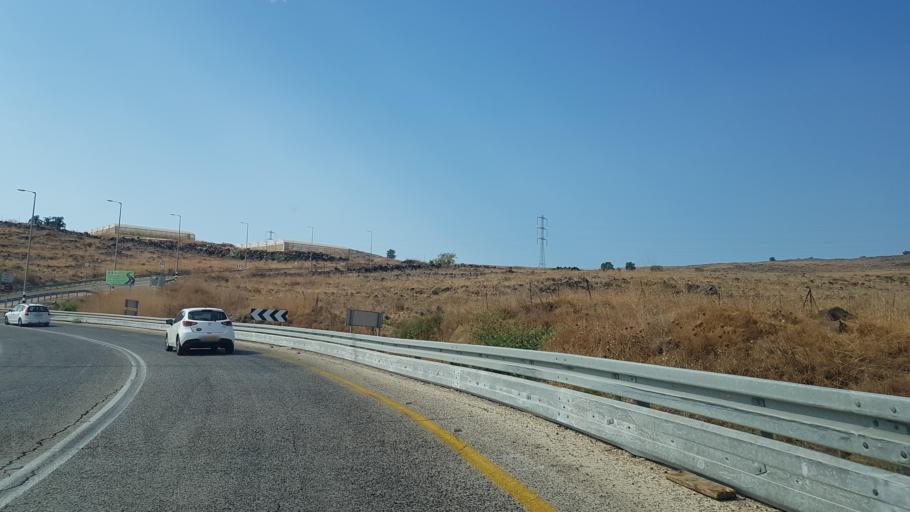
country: SY
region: Quneitra
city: Al Butayhah
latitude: 32.9142
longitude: 35.5887
